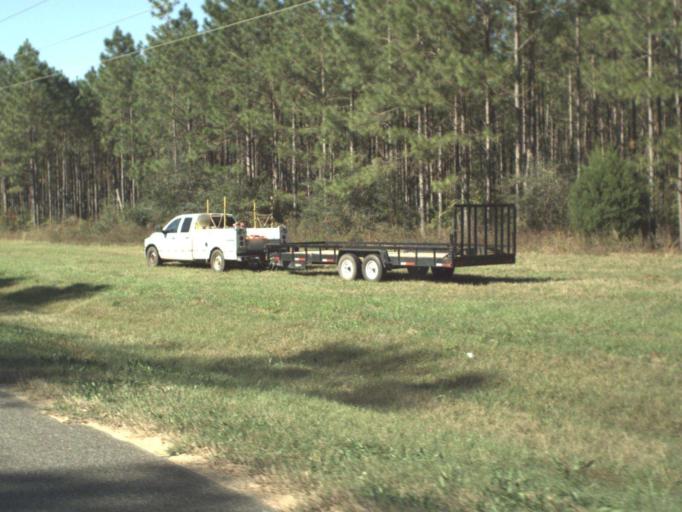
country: US
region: Florida
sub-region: Okaloosa County
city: Crestview
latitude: 30.7990
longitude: -86.6960
